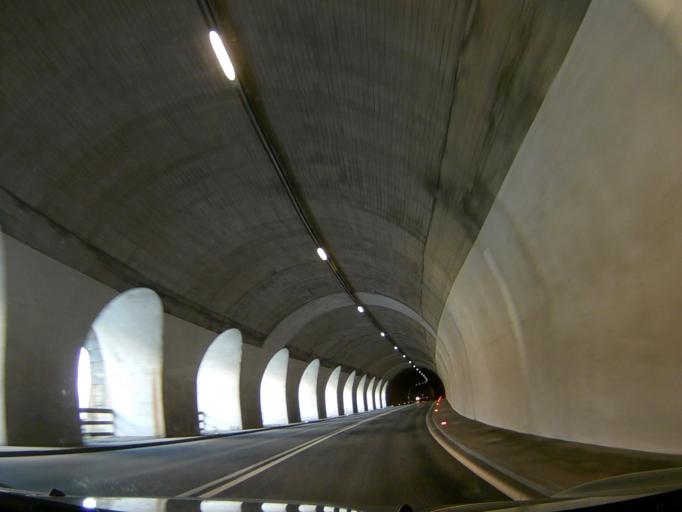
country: AT
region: Tyrol
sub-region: Politischer Bezirk Schwaz
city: Achenkirch
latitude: 47.4766
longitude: 11.7119
